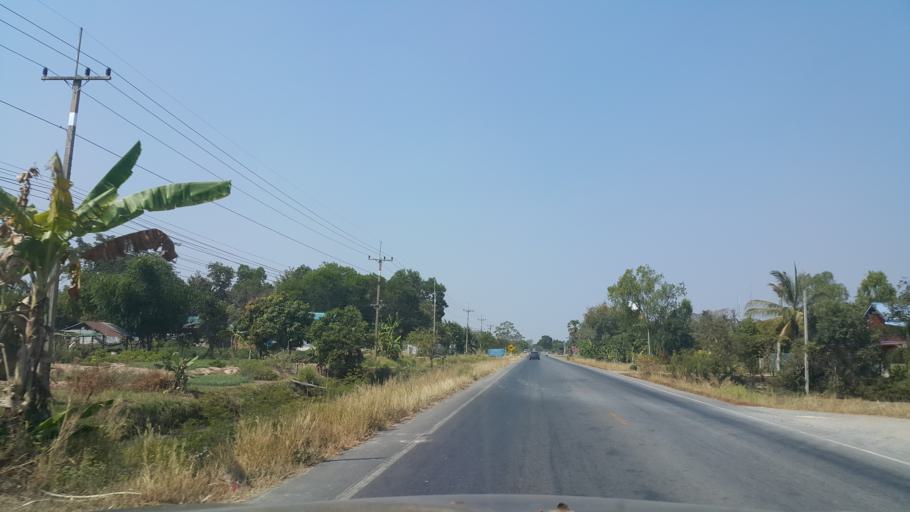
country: TH
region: Buriram
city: Khaen Dong
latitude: 15.3010
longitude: 103.1807
